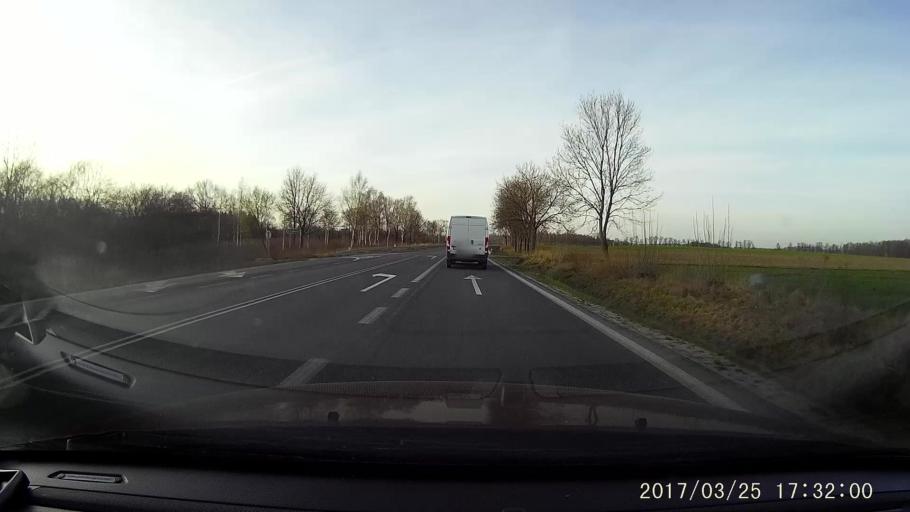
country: PL
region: Lower Silesian Voivodeship
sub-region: Powiat zgorzelecki
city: Zgorzelec
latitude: 51.1099
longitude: 15.0150
